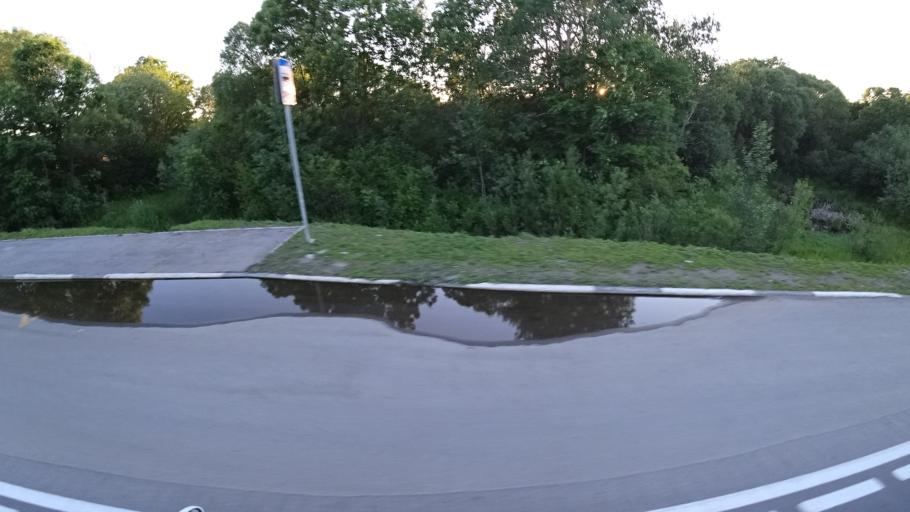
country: RU
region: Khabarovsk Krai
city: Khor
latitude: 47.8561
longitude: 134.9620
